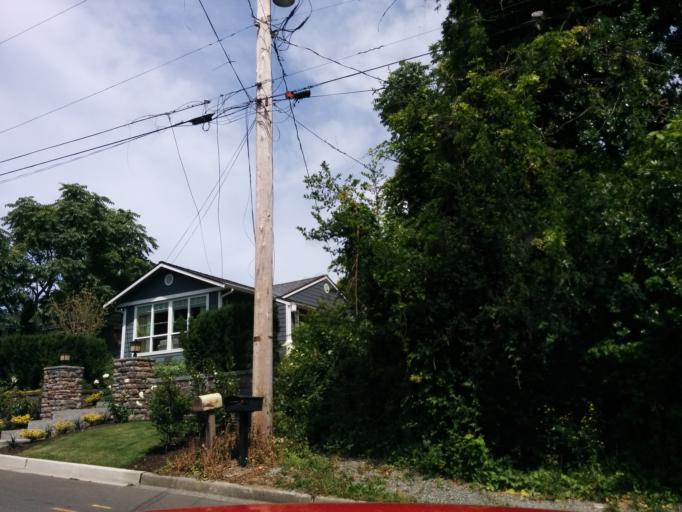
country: US
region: Washington
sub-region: King County
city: Kirkland
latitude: 47.6822
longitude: -122.2056
